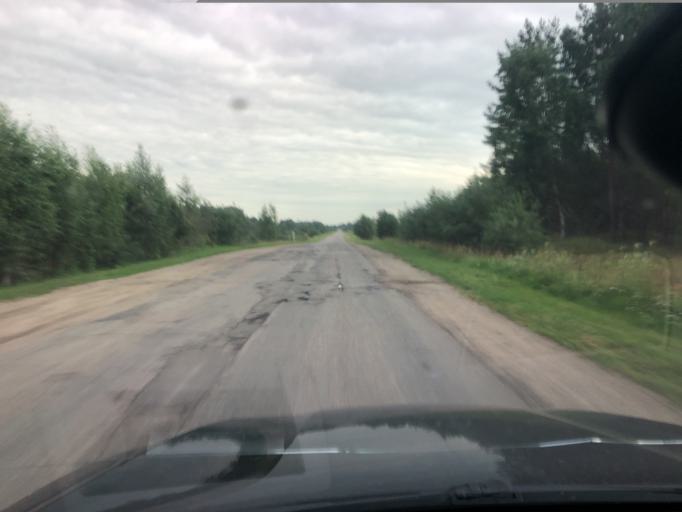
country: RU
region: Jaroslavl
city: Petrovsk
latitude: 57.0032
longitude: 39.0244
